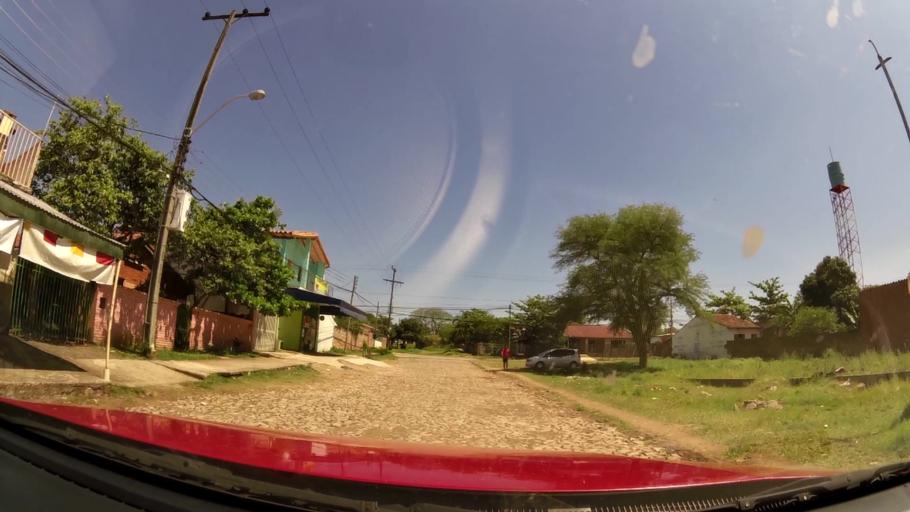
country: PY
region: Central
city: Colonia Mariano Roque Alonso
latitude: -25.2397
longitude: -57.5524
